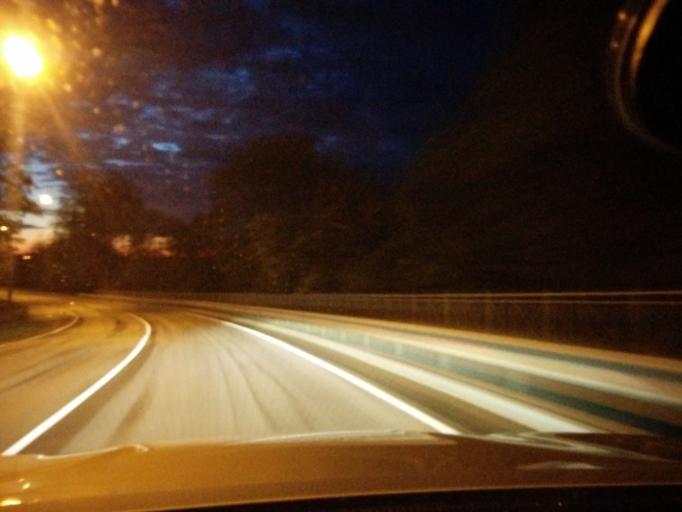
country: RU
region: Leningrad
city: Verkhniye Osel'ki
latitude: 60.2437
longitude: 30.4451
